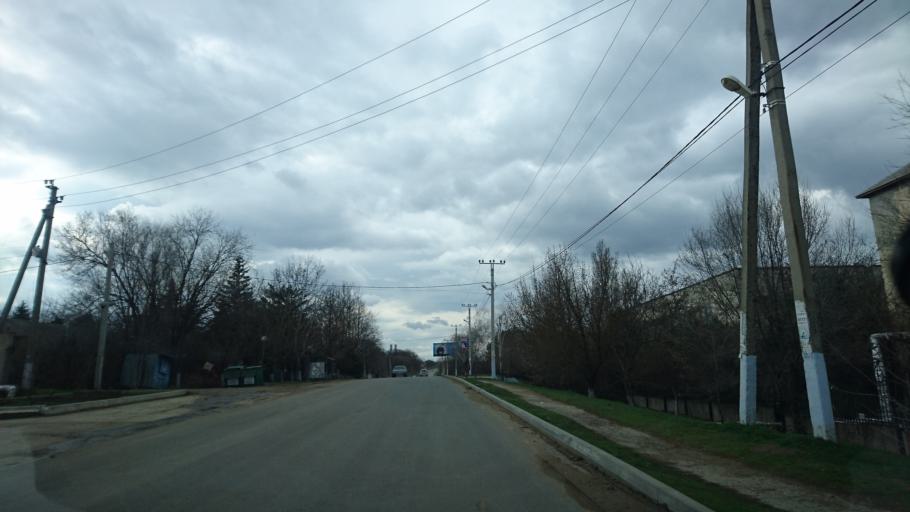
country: MD
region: Gagauzia
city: Comrat
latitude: 46.3037
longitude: 28.6356
